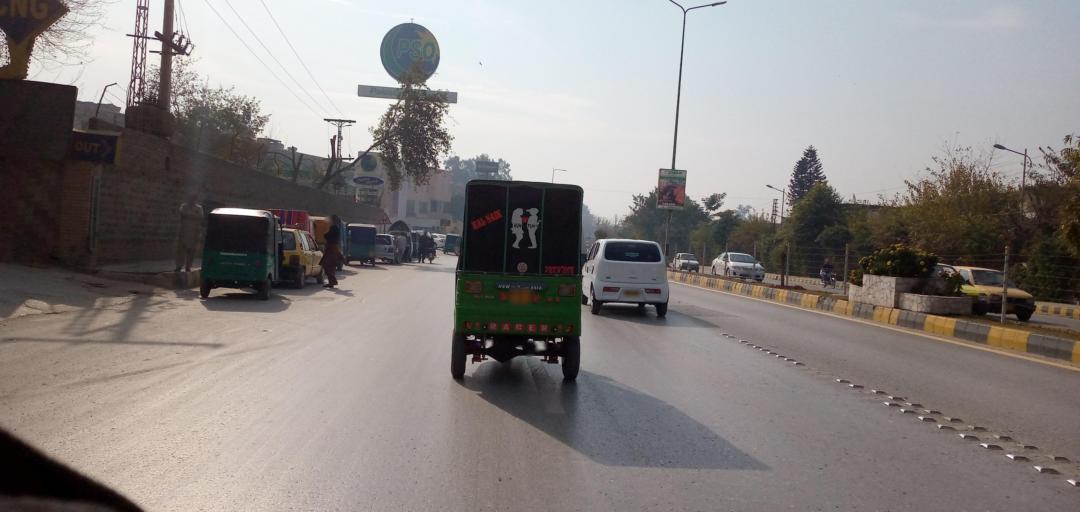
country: PK
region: Khyber Pakhtunkhwa
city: Peshawar
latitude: 34.0112
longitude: 71.5398
